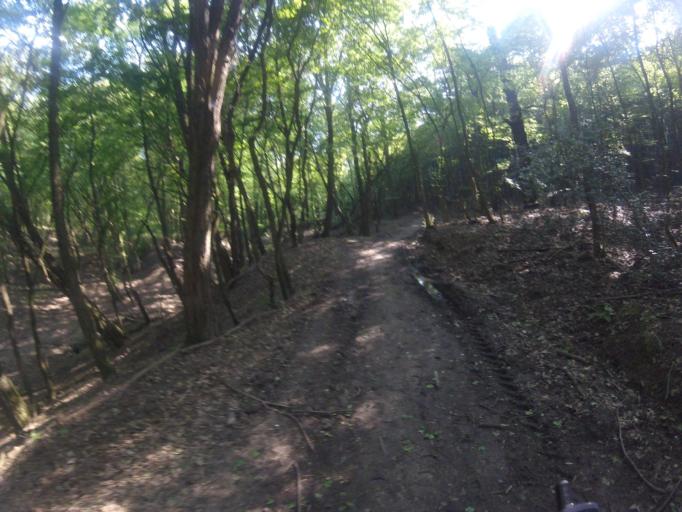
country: HU
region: Pest
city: Nagymaros
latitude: 47.8171
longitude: 18.9348
